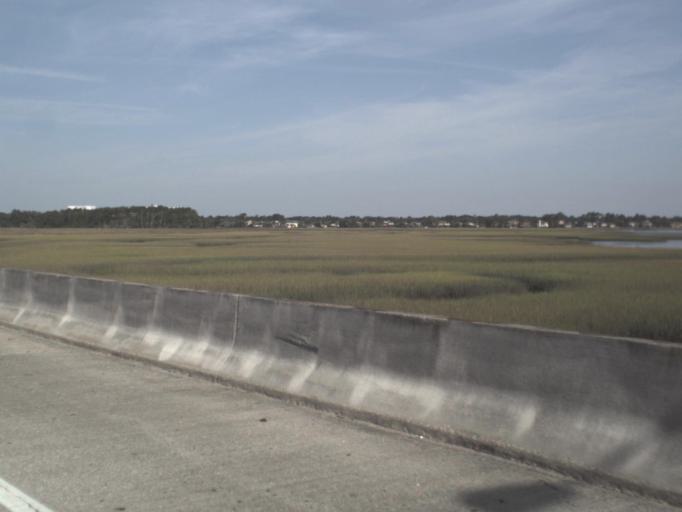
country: US
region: Florida
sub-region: Saint Johns County
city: Ponte Vedra Beach
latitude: 30.2580
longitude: -81.4194
